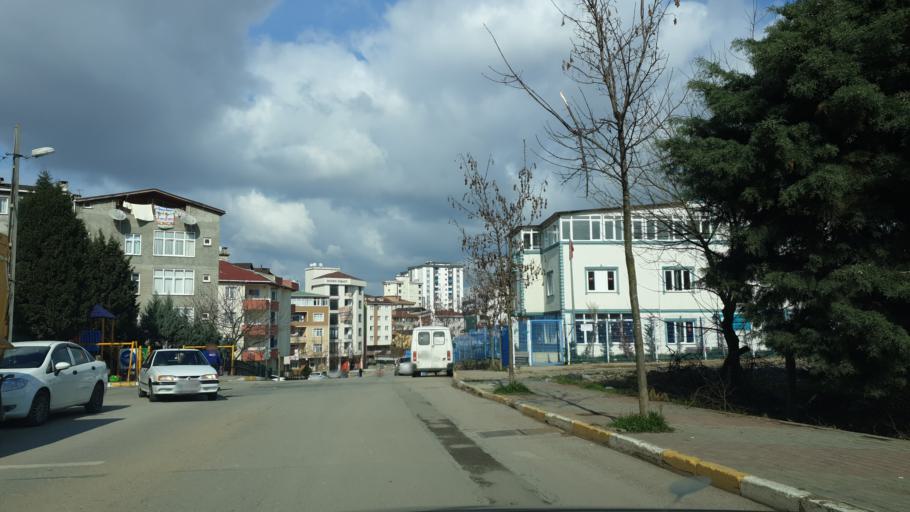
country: TR
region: Istanbul
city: Icmeler
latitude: 40.8657
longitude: 29.3092
